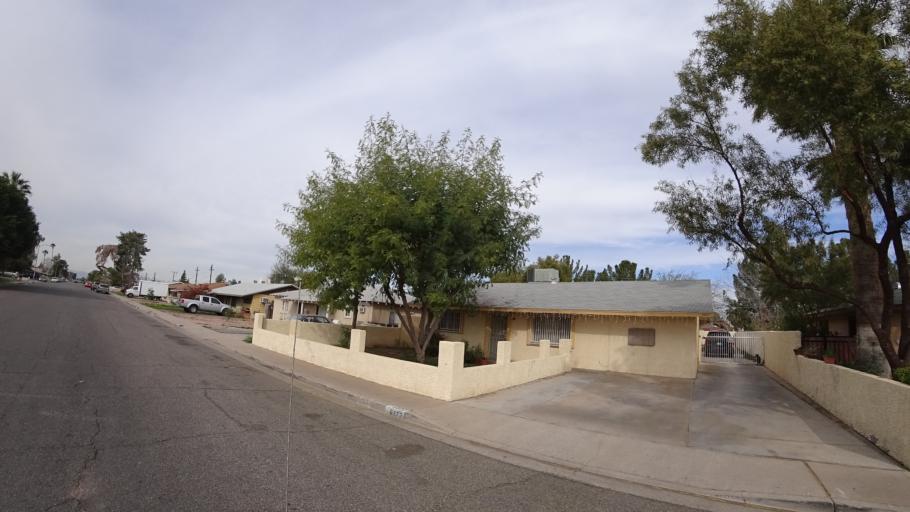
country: US
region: Arizona
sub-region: Maricopa County
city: Glendale
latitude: 33.5348
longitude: -112.1959
